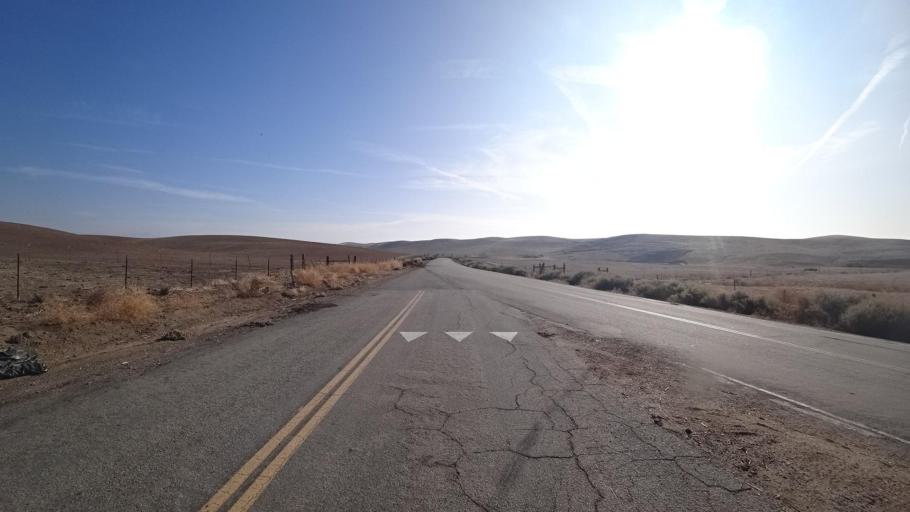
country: US
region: California
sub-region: Tulare County
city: Richgrove
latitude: 35.6209
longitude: -119.0288
